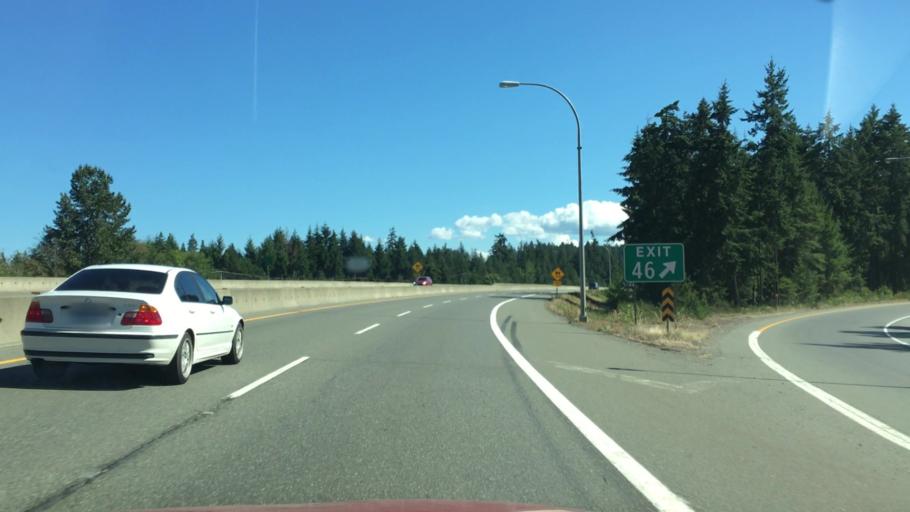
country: CA
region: British Columbia
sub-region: Regional District of Nanaimo
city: Parksville
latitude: 49.3002
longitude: -124.2571
